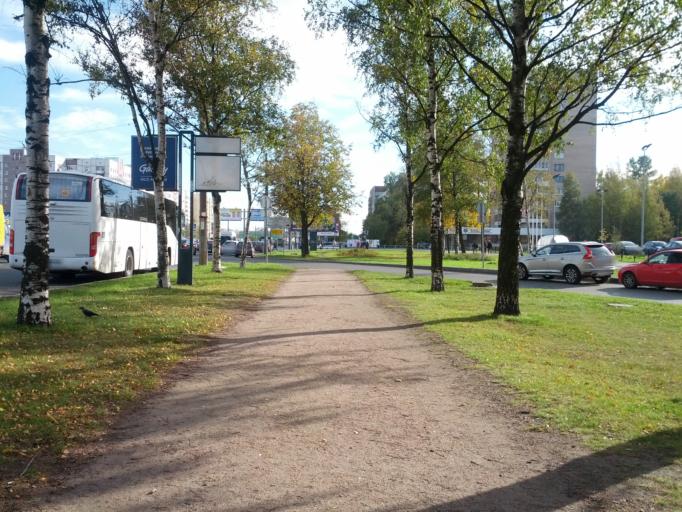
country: RU
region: Leningrad
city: Rybatskoye
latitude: 59.9012
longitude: 30.4875
